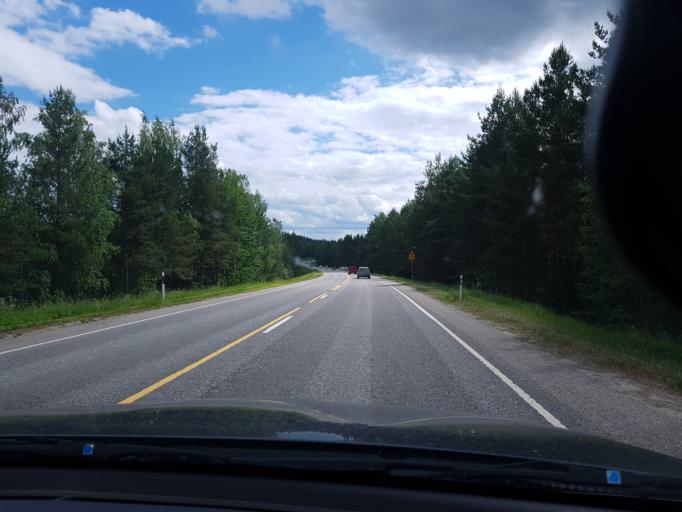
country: FI
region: Pirkanmaa
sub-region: Tampere
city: Paelkaene
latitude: 61.3112
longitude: 24.2889
